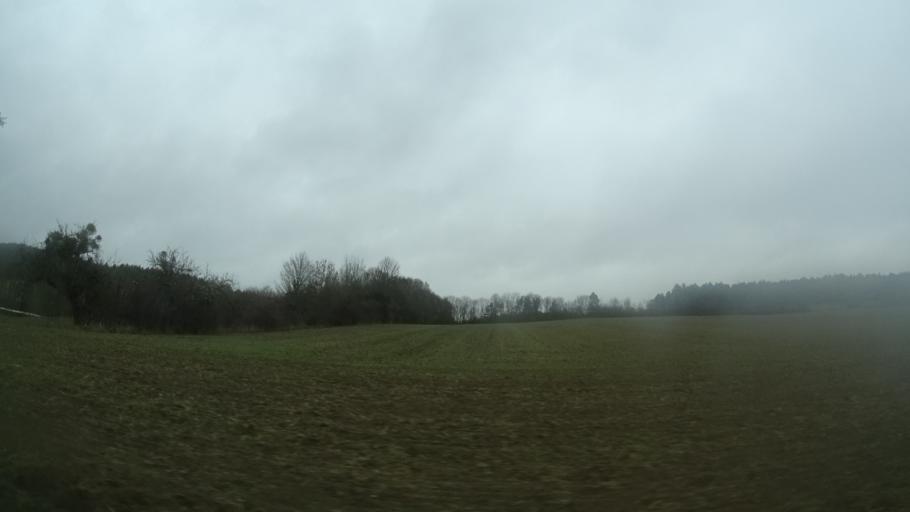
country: DE
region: Thuringia
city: Romhild
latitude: 50.4231
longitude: 10.5431
